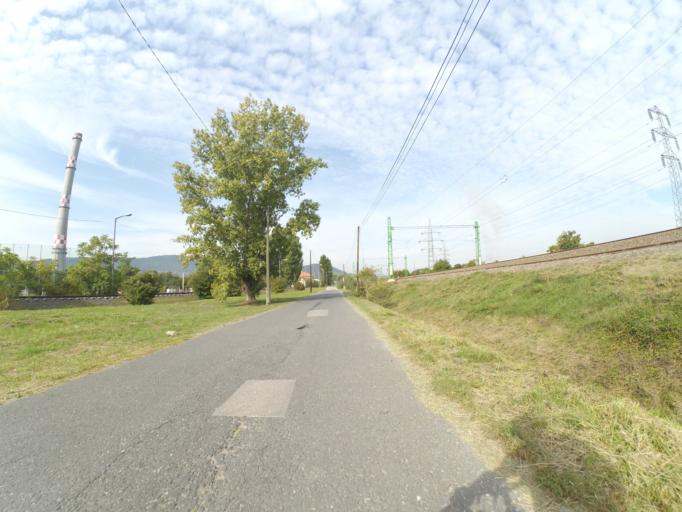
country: HU
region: Budapest
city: Budapest III. keruelet
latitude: 47.5666
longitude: 19.0421
